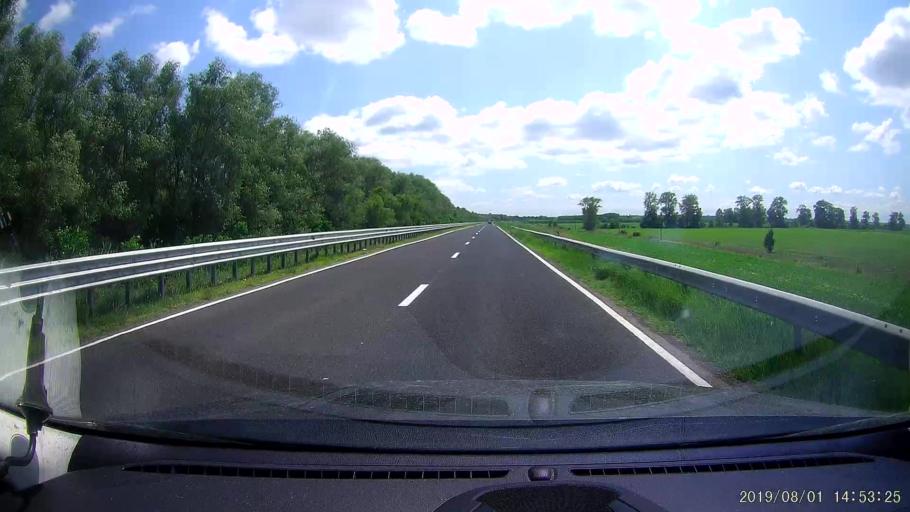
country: RO
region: Braila
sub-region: Municipiul Braila
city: Braila
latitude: 45.3360
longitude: 28.0031
